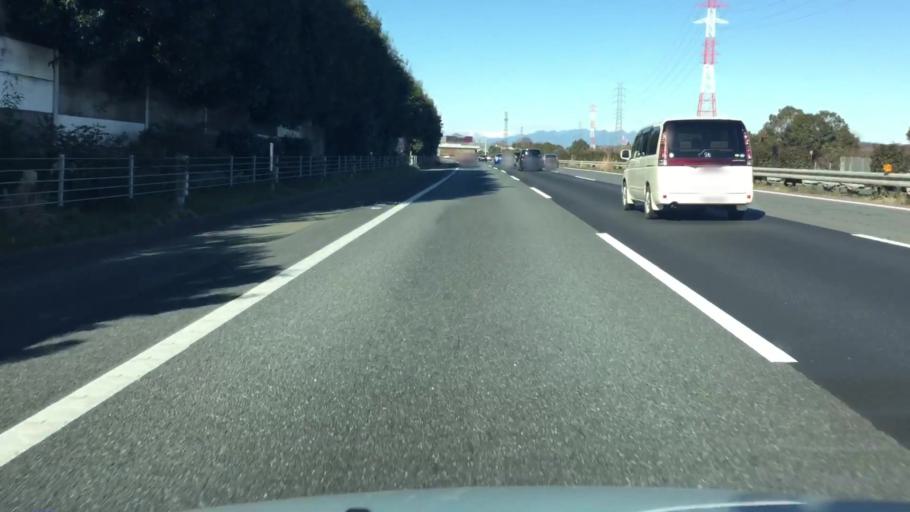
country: JP
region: Saitama
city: Yorii
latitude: 36.1601
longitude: 139.2105
